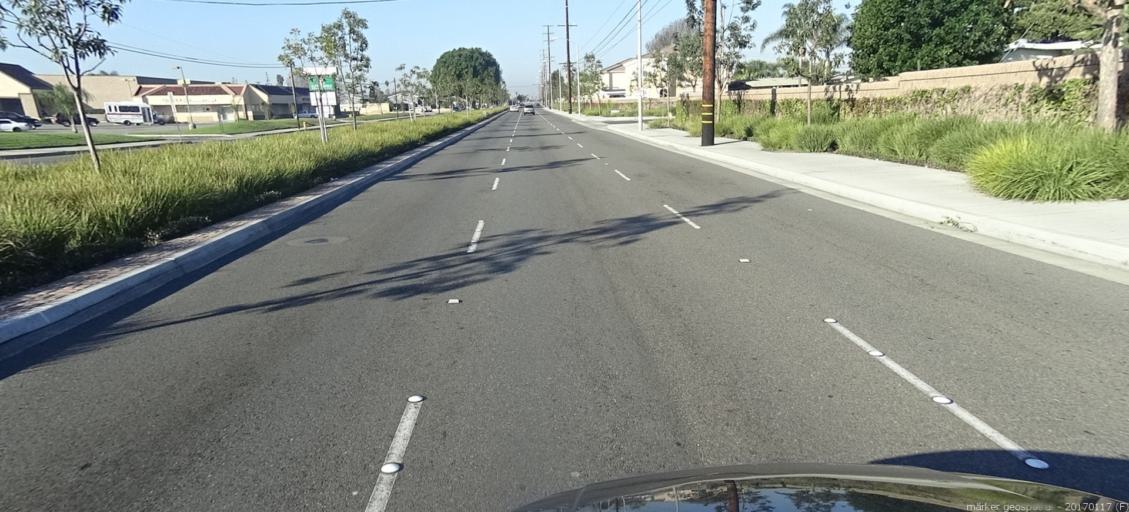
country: US
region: California
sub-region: Orange County
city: Stanton
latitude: 33.8032
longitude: -117.9601
